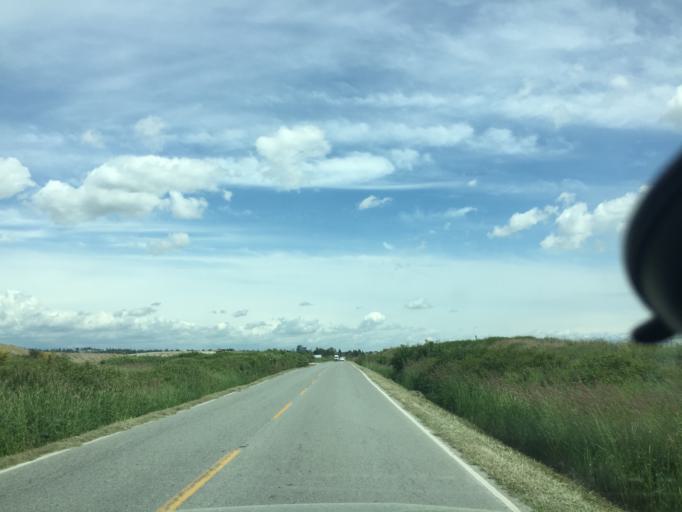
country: CA
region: British Columbia
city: Richmond
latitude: 49.2066
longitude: -123.1908
